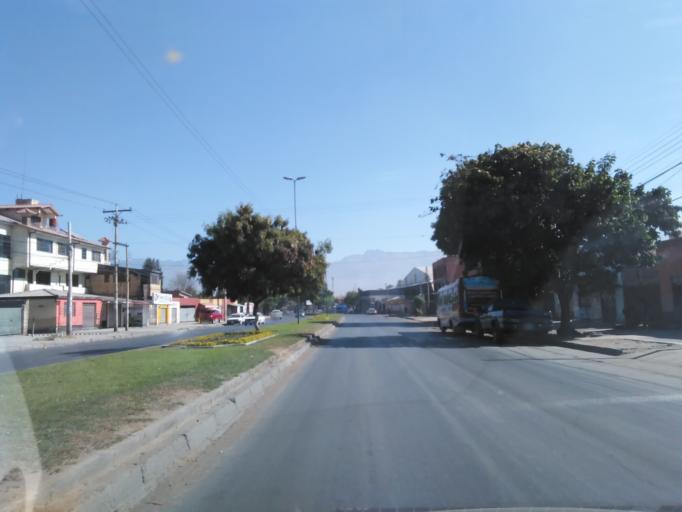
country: BO
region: Cochabamba
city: Cochabamba
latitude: -17.4080
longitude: -66.1753
